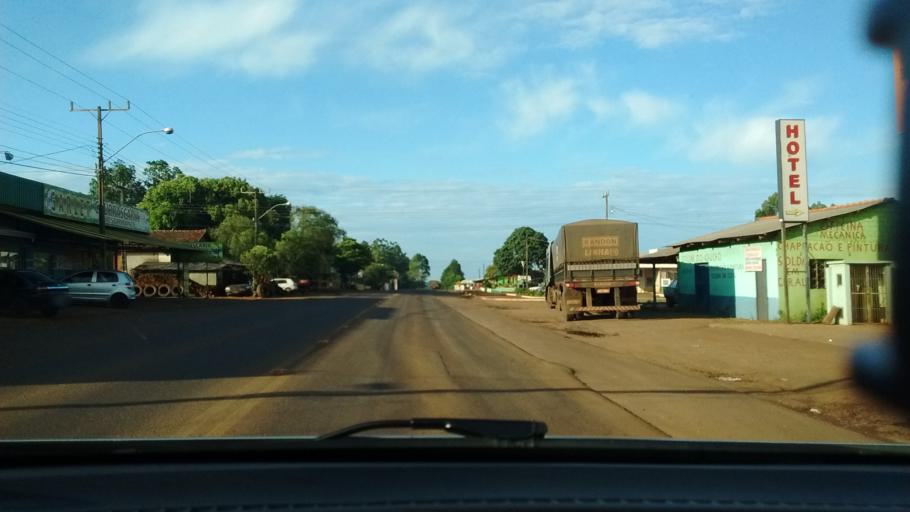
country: BR
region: Parana
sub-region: Cascavel
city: Cascavel
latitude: -25.1417
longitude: -53.5866
